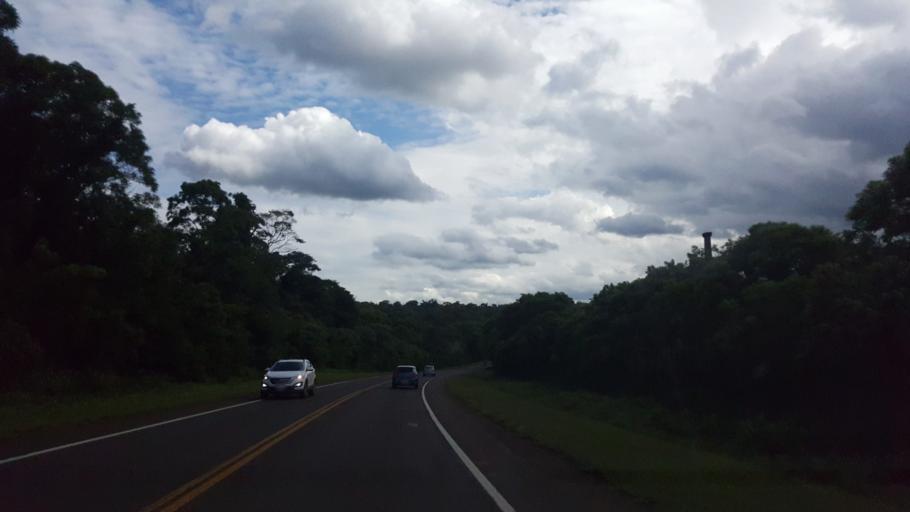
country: AR
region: Misiones
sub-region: Departamento de Iguazu
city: Puerto Iguazu
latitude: -25.7031
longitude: -54.5149
